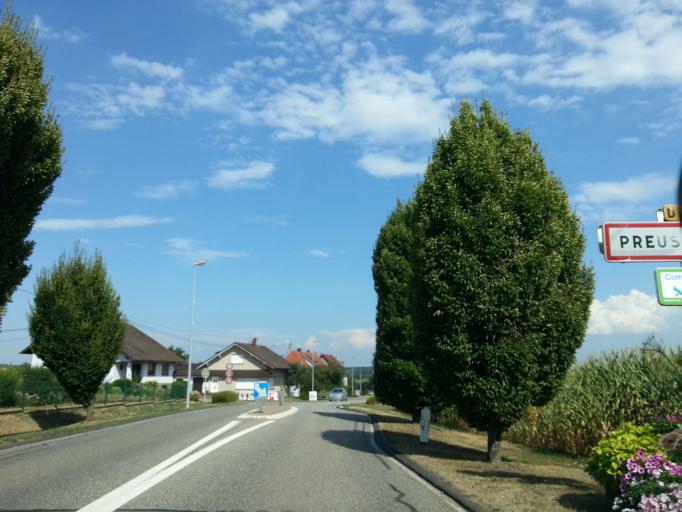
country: FR
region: Alsace
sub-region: Departement du Bas-Rhin
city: Goersdorf
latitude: 48.9407
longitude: 7.8016
